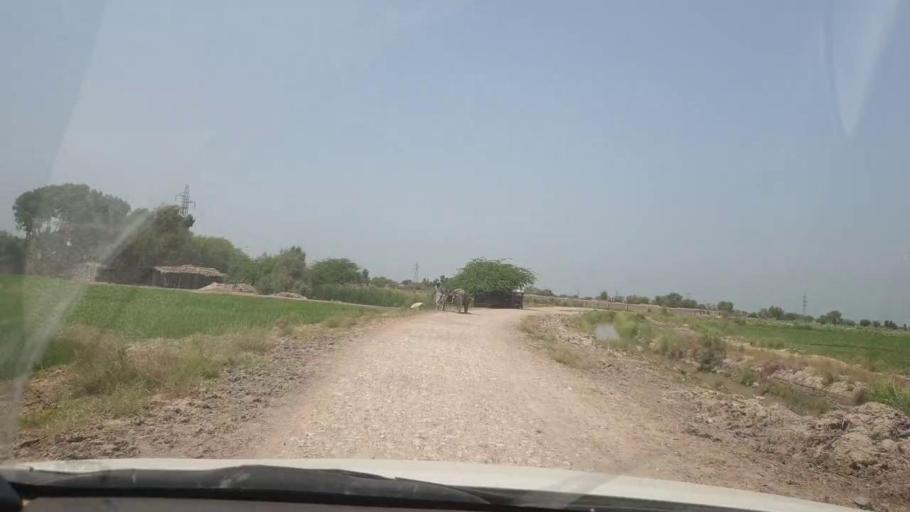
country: PK
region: Sindh
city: Lakhi
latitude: 27.8703
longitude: 68.6946
